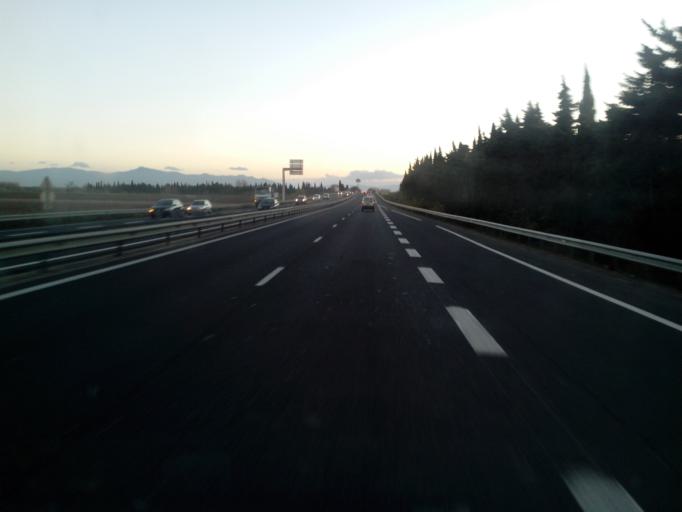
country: FR
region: Languedoc-Roussillon
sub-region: Departement des Pyrenees-Orientales
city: Rivesaltes
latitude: 42.7764
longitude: 2.9028
